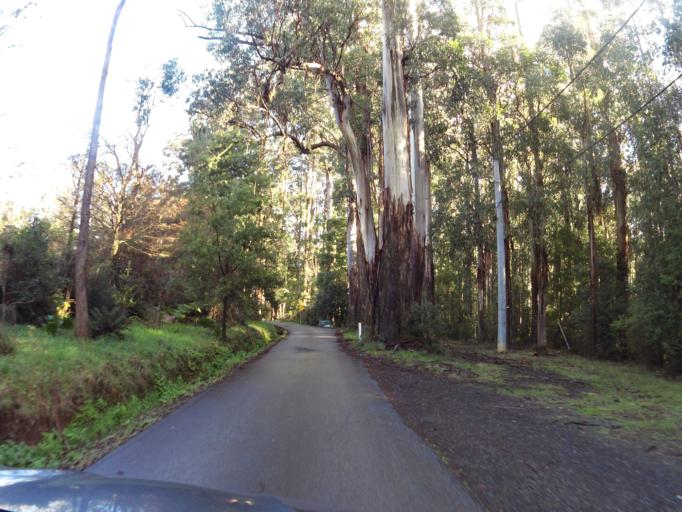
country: AU
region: Victoria
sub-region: Yarra Ranges
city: Kallista
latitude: -37.8836
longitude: 145.3590
